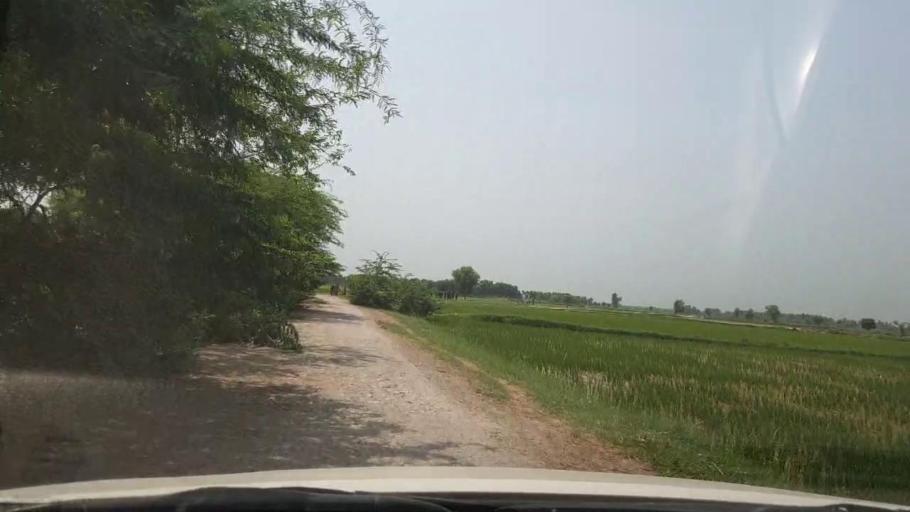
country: PK
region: Sindh
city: Shikarpur
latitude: 27.9835
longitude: 68.7177
